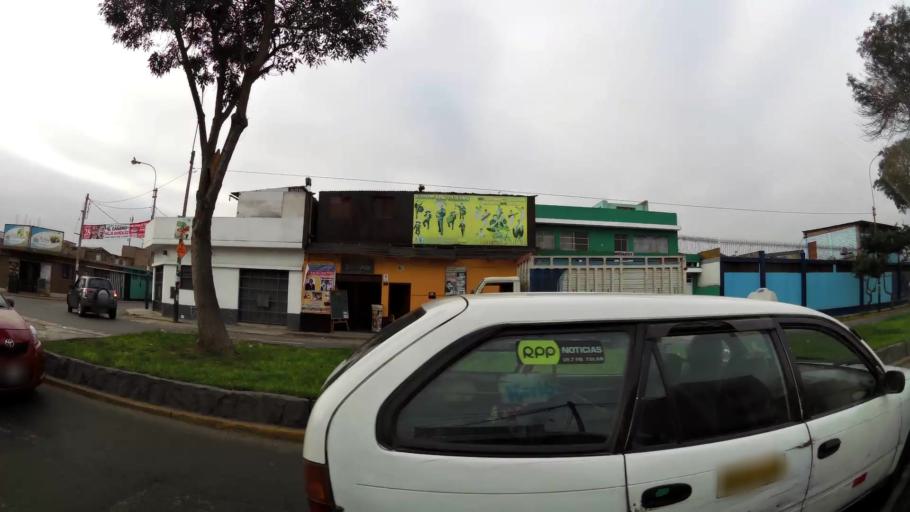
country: PE
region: Lima
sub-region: Lima
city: Surco
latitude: -12.1444
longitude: -77.0148
